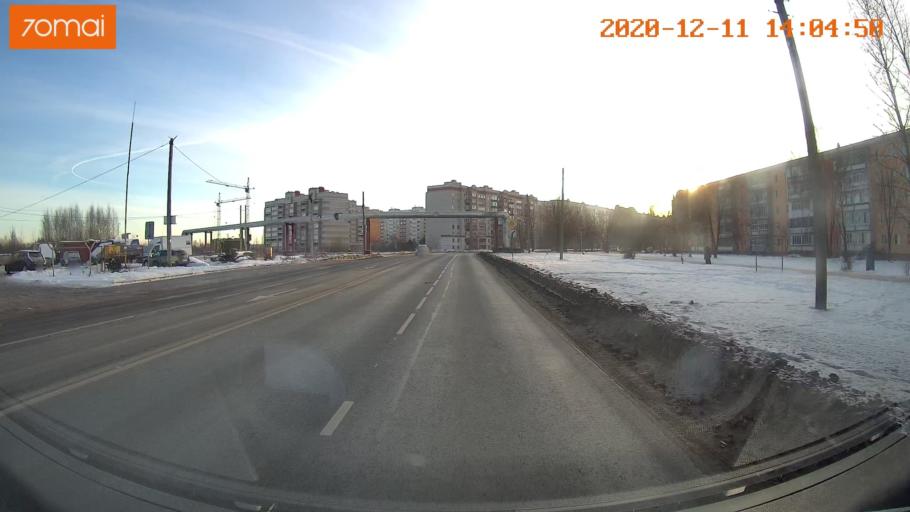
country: RU
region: Kostroma
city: Oktyabr'skiy
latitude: 57.7515
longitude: 41.0163
